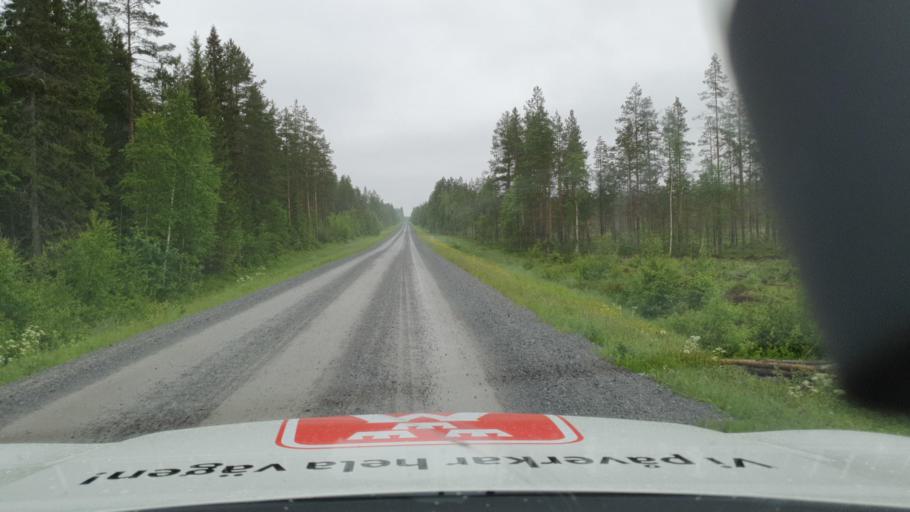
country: SE
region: Vaesterbotten
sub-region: Nordmalings Kommun
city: Nordmaling
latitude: 63.8207
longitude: 19.4940
